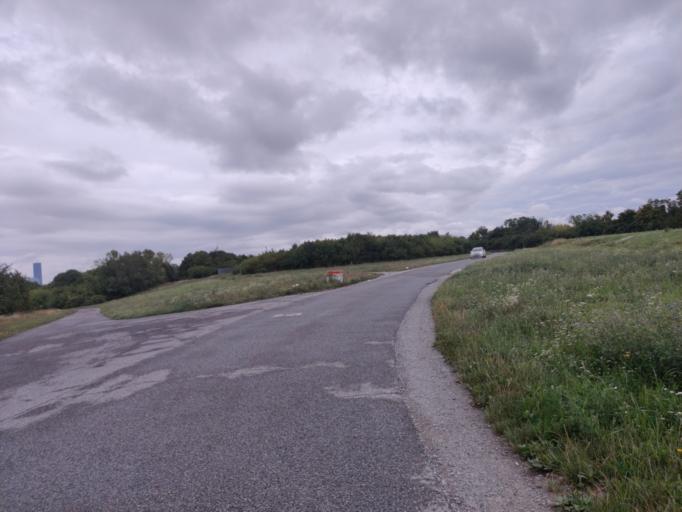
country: AT
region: Lower Austria
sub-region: Politischer Bezirk Korneuburg
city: Langenzersdorf
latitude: 48.2674
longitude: 16.3713
